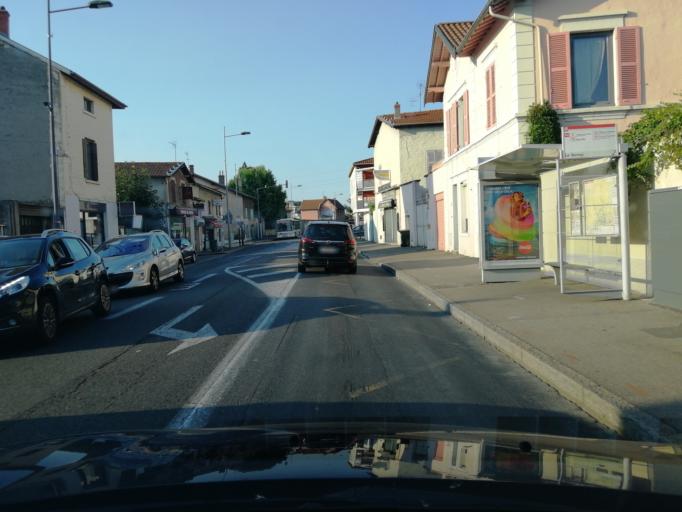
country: FR
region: Rhone-Alpes
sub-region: Departement du Rhone
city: Sathonay-Camp
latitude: 45.8093
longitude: 4.8571
